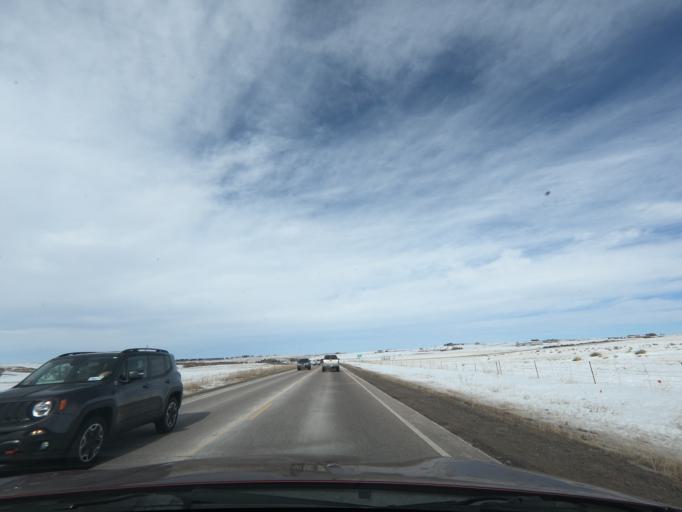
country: US
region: Colorado
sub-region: Elbert County
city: Elizabeth
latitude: 39.2212
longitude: -104.7021
